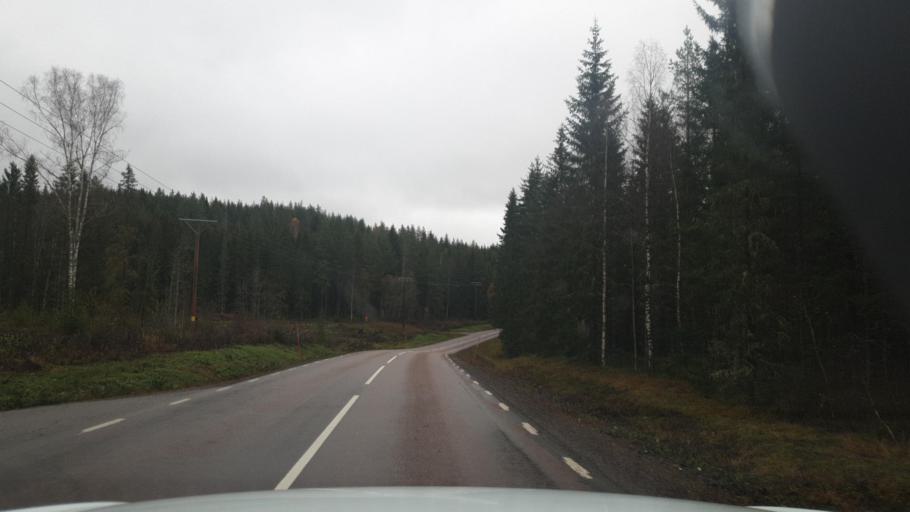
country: SE
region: Vaermland
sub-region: Eda Kommun
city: Charlottenberg
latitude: 59.8086
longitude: 12.1995
